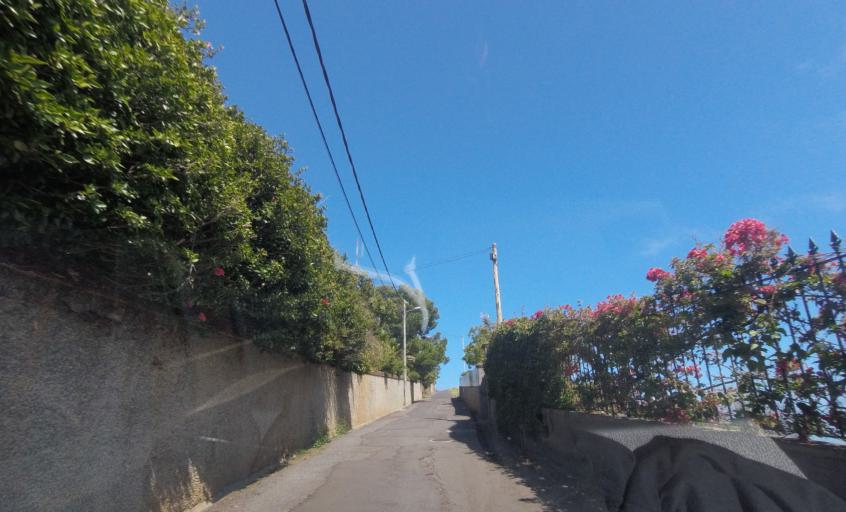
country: PT
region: Madeira
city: Camara de Lobos
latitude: 32.6428
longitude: -16.9407
